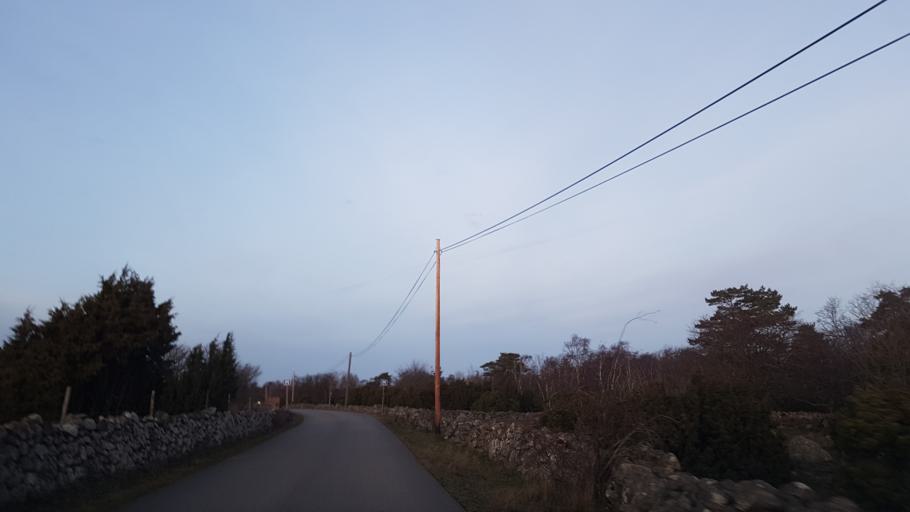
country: SE
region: Blekinge
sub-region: Karlskrona Kommun
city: Jaemjoe
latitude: 56.0831
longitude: 15.8420
